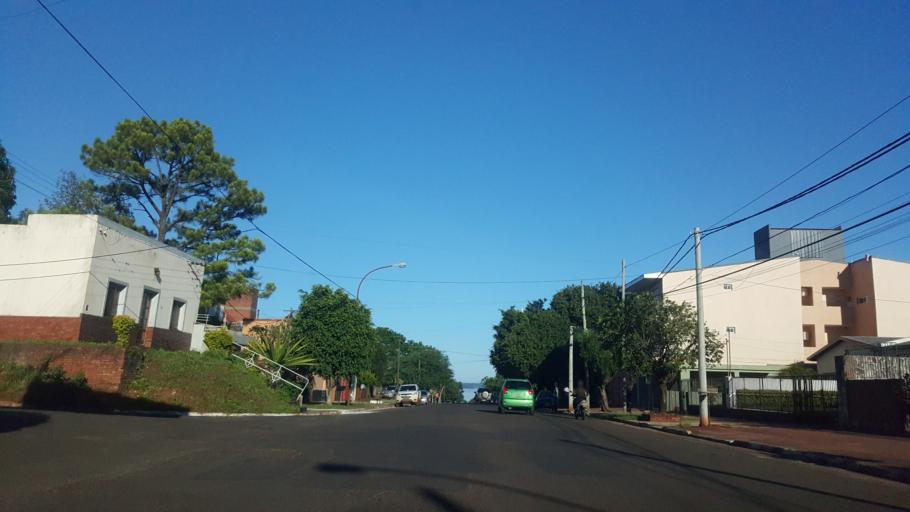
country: AR
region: Misiones
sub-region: Departamento de Capital
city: Posadas
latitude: -27.3939
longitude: -55.9047
